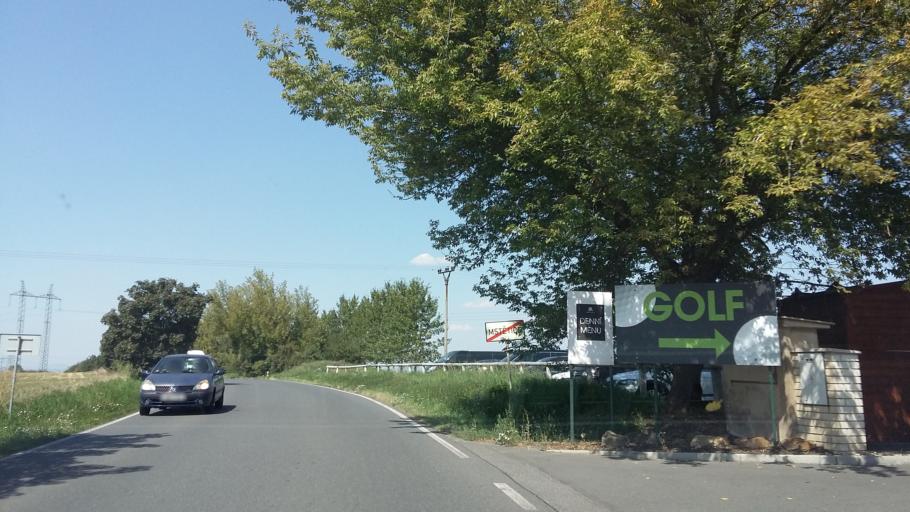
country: CZ
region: Central Bohemia
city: Jirny
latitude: 50.1439
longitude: 14.6923
